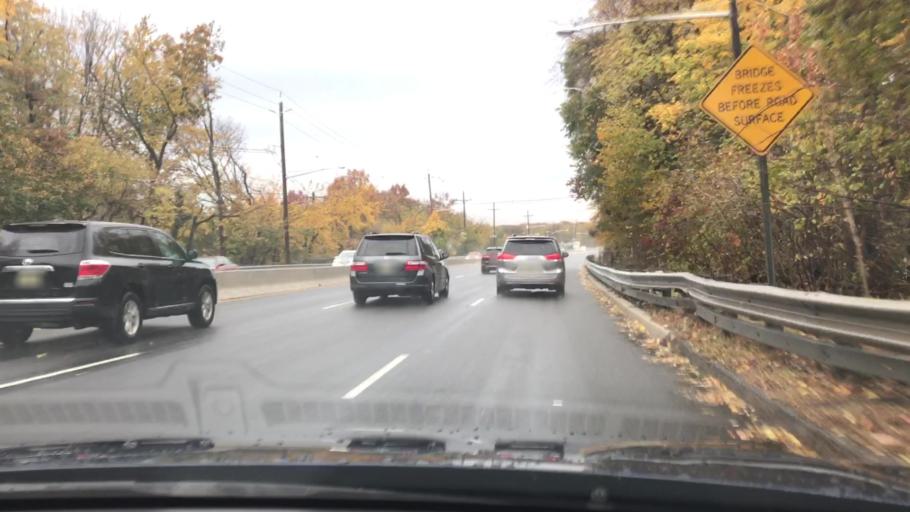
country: US
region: New Jersey
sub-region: Bergen County
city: Teaneck
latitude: 40.8990
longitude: -74.0257
